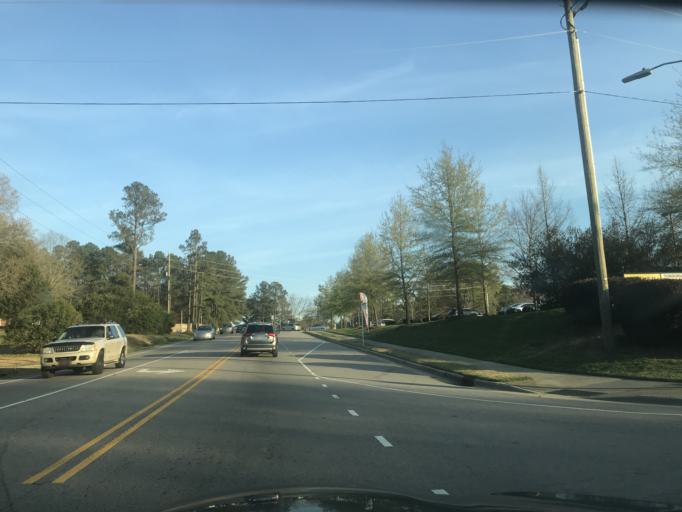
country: US
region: North Carolina
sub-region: Wake County
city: Garner
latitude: 35.7329
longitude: -78.5600
